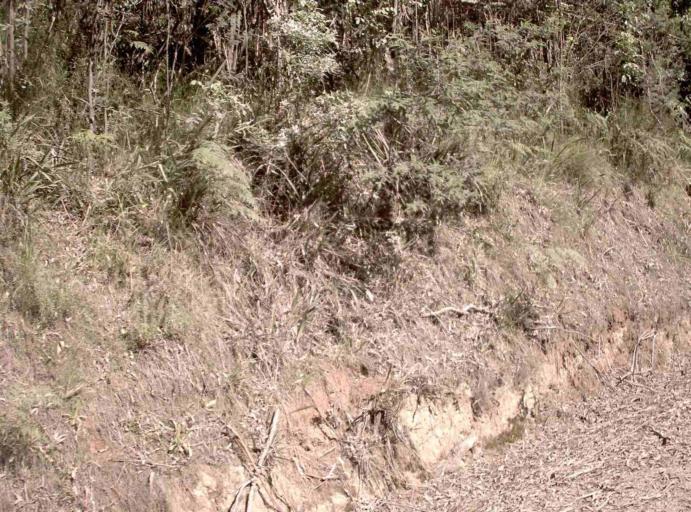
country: AU
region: New South Wales
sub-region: Bombala
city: Bombala
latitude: -37.2200
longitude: 148.7471
